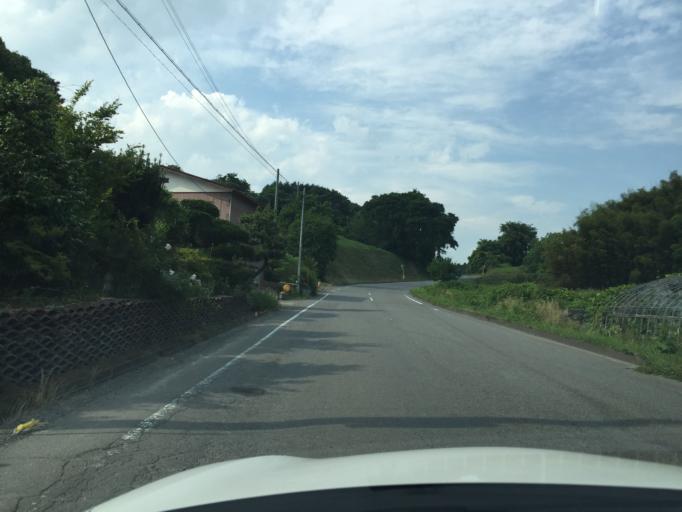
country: JP
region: Fukushima
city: Miharu
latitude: 37.4126
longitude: 140.4526
